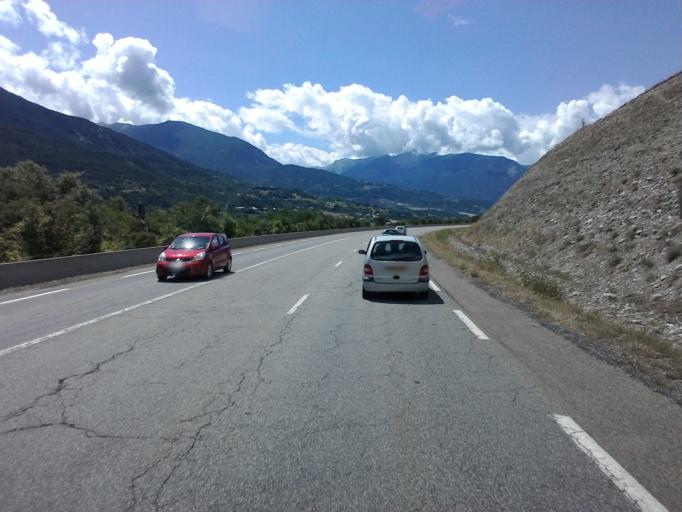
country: FR
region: Provence-Alpes-Cote d'Azur
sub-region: Departement des Hautes-Alpes
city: Embrun
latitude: 44.6068
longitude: 6.5291
